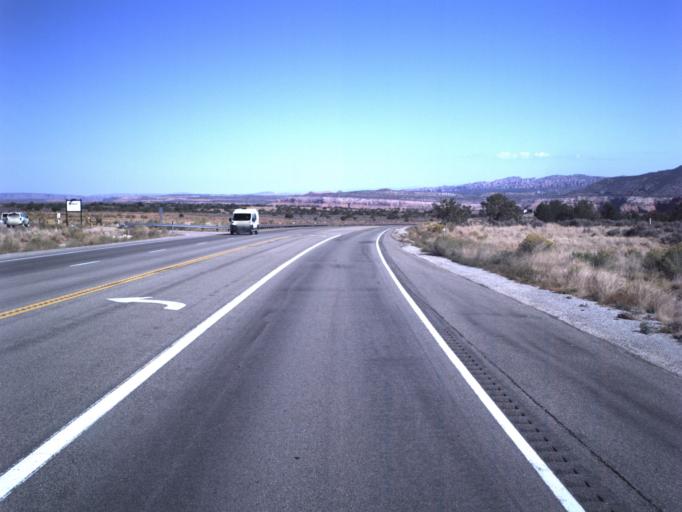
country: US
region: Utah
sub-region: Grand County
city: Moab
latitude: 38.3266
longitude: -109.4284
